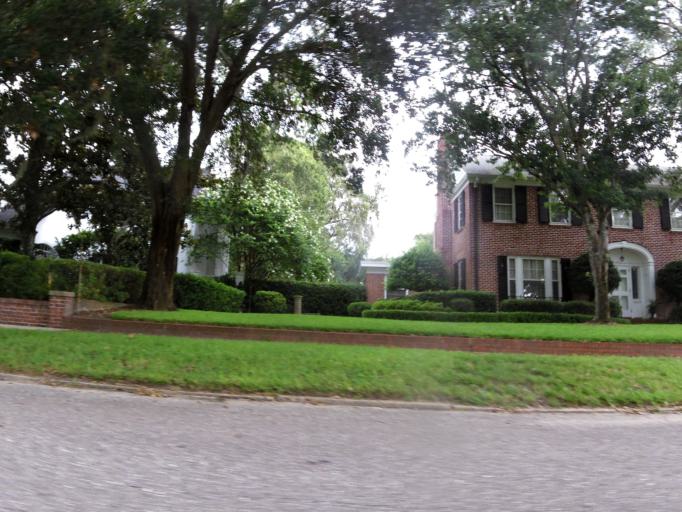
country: US
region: Florida
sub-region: Duval County
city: Jacksonville
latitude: 30.2913
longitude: -81.7068
